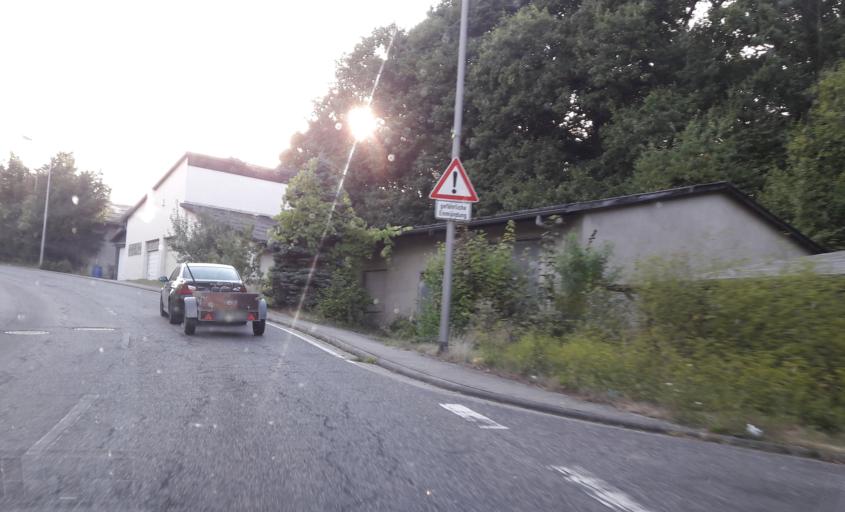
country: DE
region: Rheinland-Pfalz
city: Briedel
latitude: 50.0337
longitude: 7.1585
